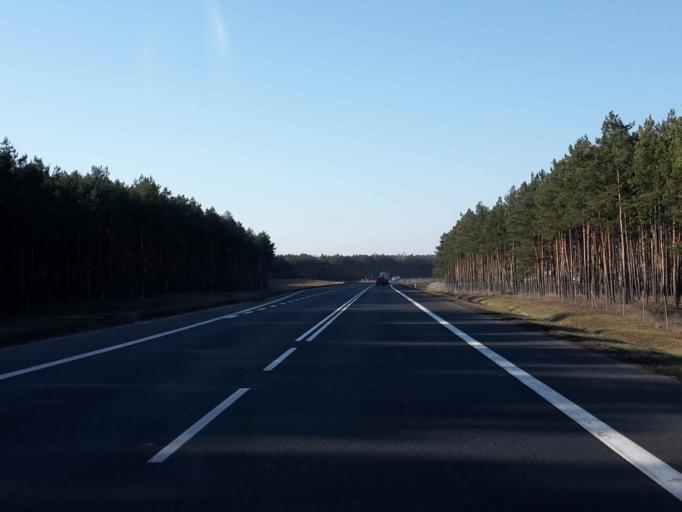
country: PL
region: Kujawsko-Pomorskie
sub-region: Torun
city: Torun
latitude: 52.9734
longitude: 18.5682
